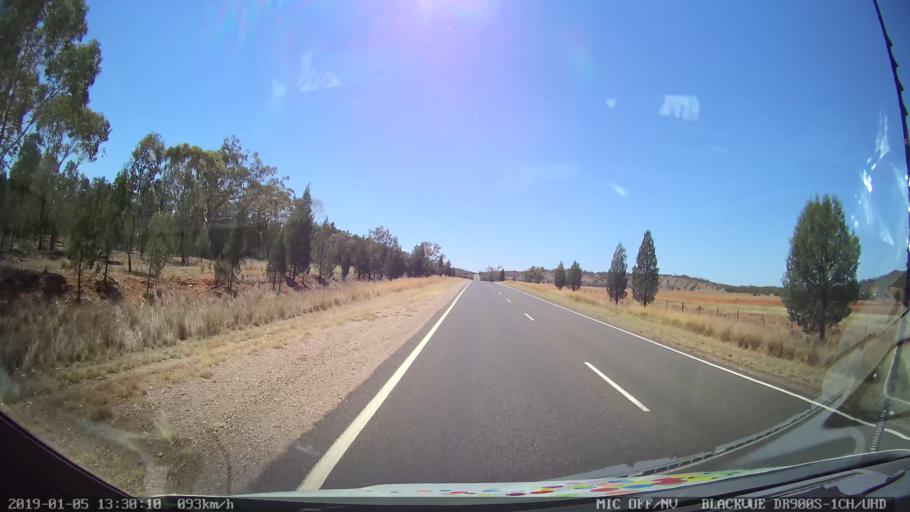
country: AU
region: New South Wales
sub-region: Gunnedah
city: Gunnedah
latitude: -31.0212
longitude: 150.0669
